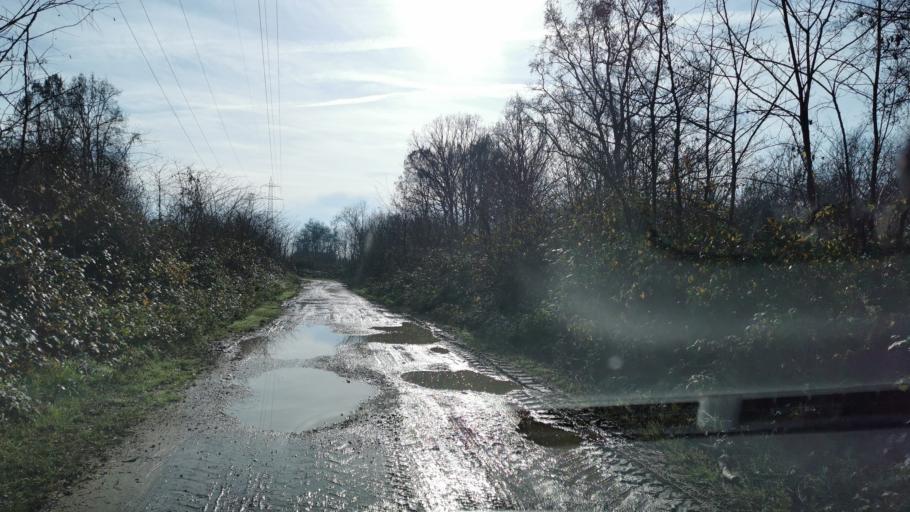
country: IT
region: Piedmont
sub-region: Provincia di Torino
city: Bosconero
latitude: 45.2772
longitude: 7.7739
